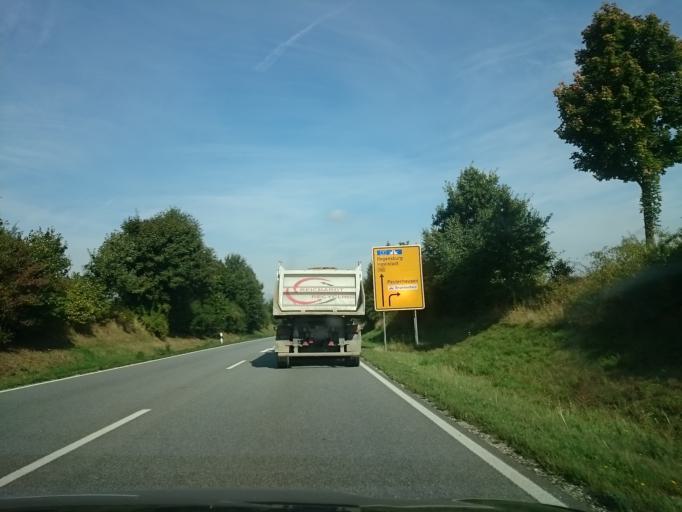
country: DE
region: Bavaria
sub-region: Upper Bavaria
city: Gachenbach
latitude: 48.5260
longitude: 11.2398
